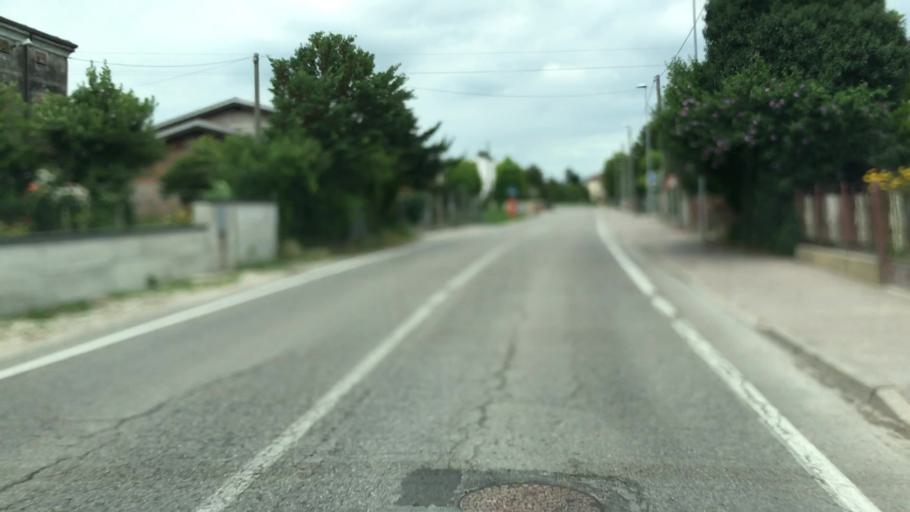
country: IT
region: Lombardy
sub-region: Provincia di Mantova
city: Quistello
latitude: 45.0315
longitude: 11.0067
